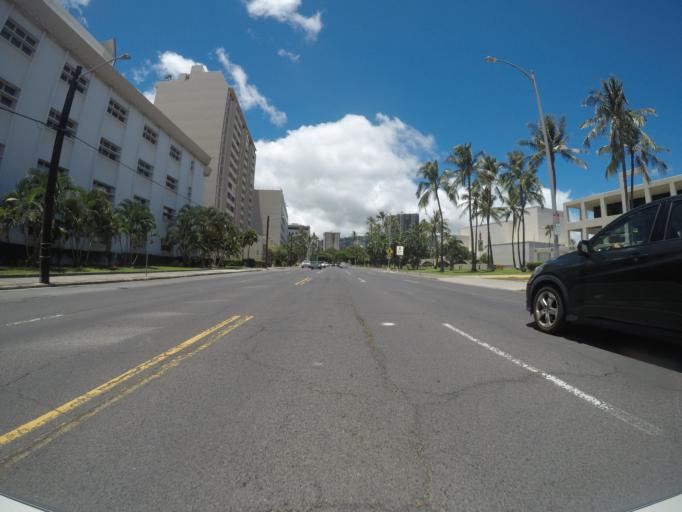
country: US
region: Hawaii
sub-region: Honolulu County
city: Honolulu
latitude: 21.3006
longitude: -157.8514
